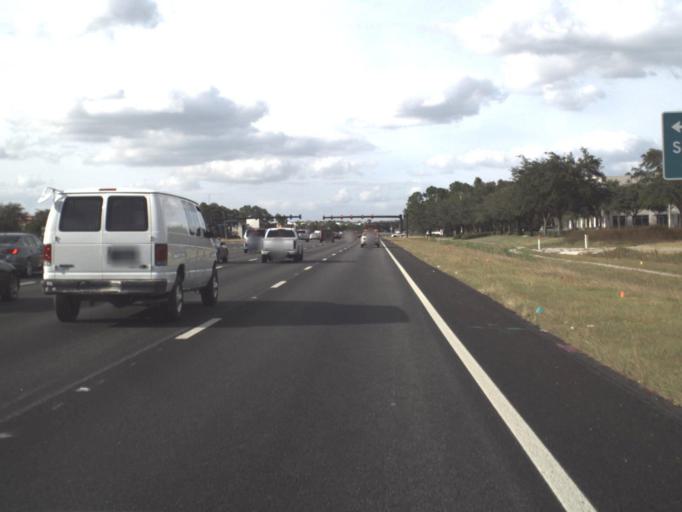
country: US
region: Florida
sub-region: Orange County
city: Williamsburg
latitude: 28.4365
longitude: -81.4246
